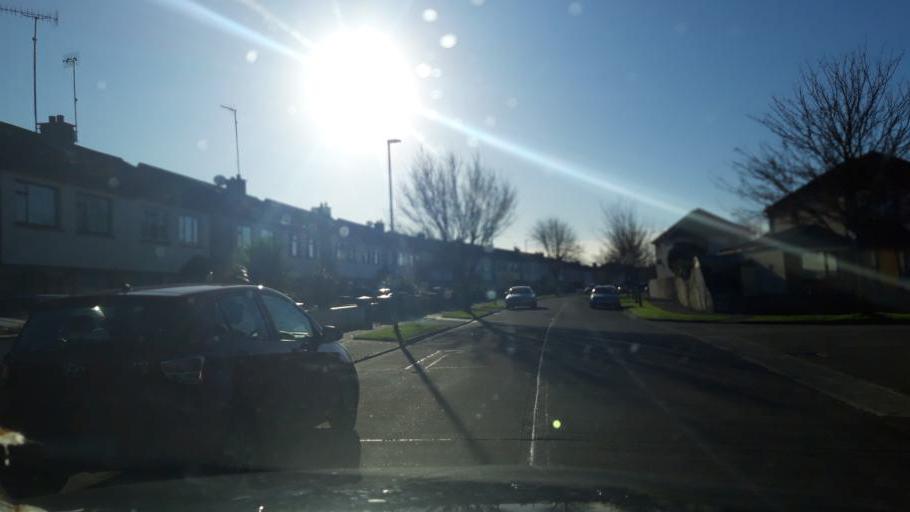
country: IE
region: Leinster
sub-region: Fingal County
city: Swords
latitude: 53.4551
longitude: -6.2485
